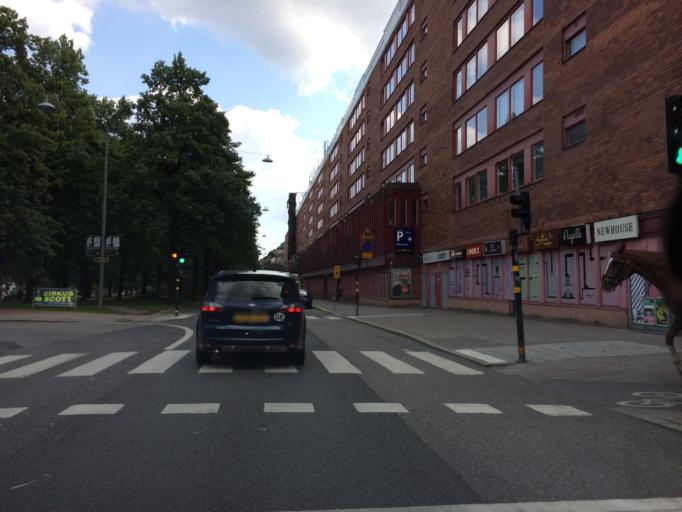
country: SE
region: Stockholm
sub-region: Stockholms Kommun
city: OEstermalm
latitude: 59.3407
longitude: 18.0900
